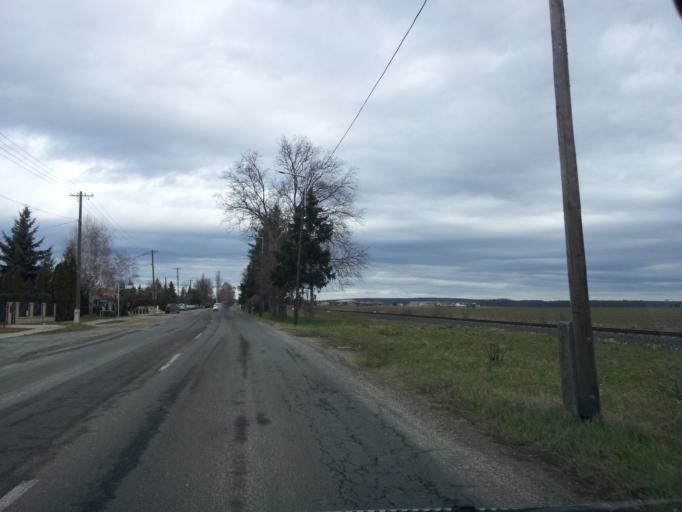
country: HU
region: Vas
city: Gencsapati
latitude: 47.3306
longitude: 16.5838
